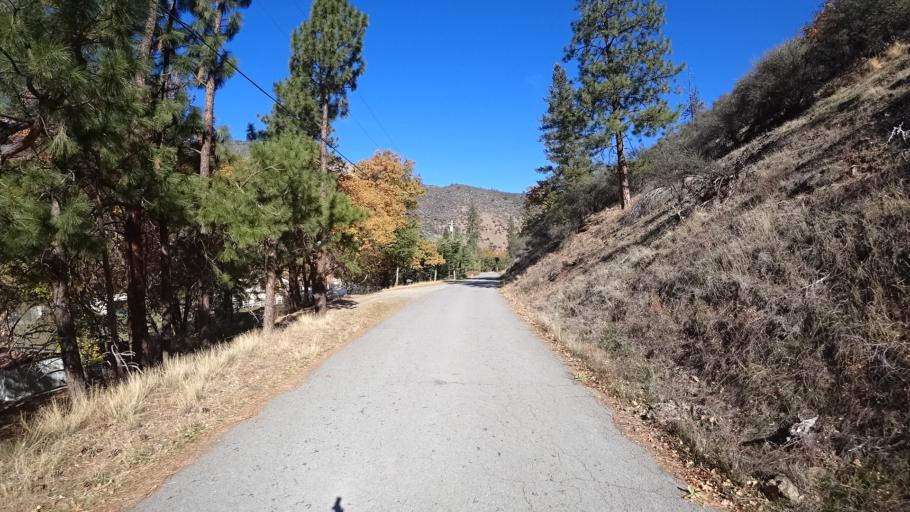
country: US
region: California
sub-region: Siskiyou County
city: Yreka
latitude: 41.8320
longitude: -122.6388
